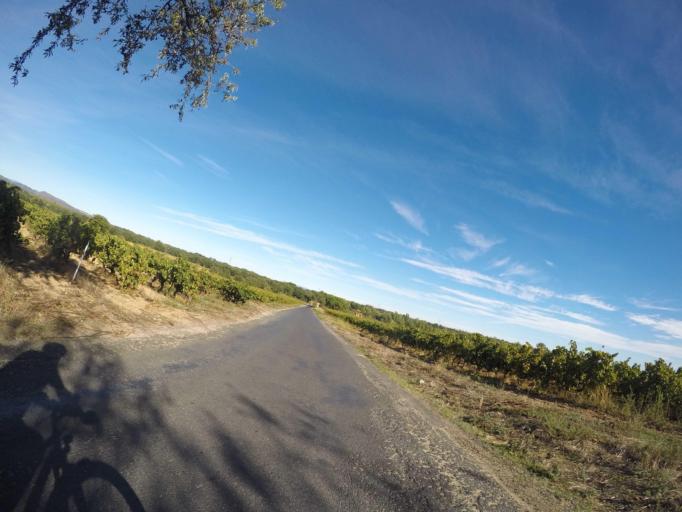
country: FR
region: Languedoc-Roussillon
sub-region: Departement des Pyrenees-Orientales
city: Trouillas
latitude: 42.5839
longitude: 2.8103
